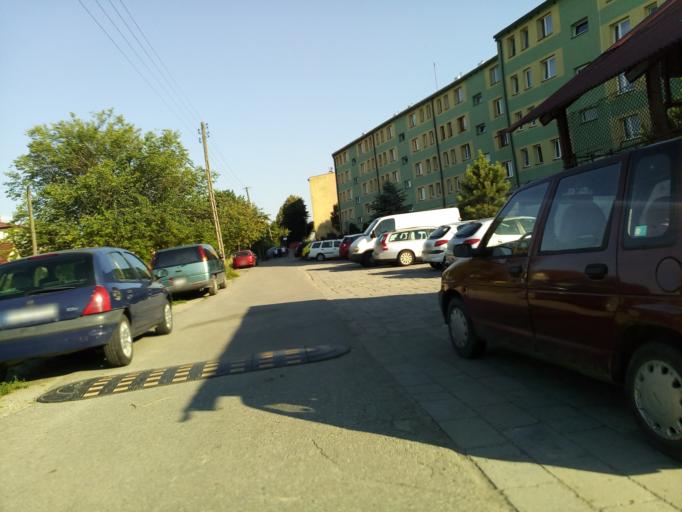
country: PL
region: Lesser Poland Voivodeship
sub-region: Powiat nowosadecki
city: Stary Sacz
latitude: 49.5693
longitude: 20.6274
